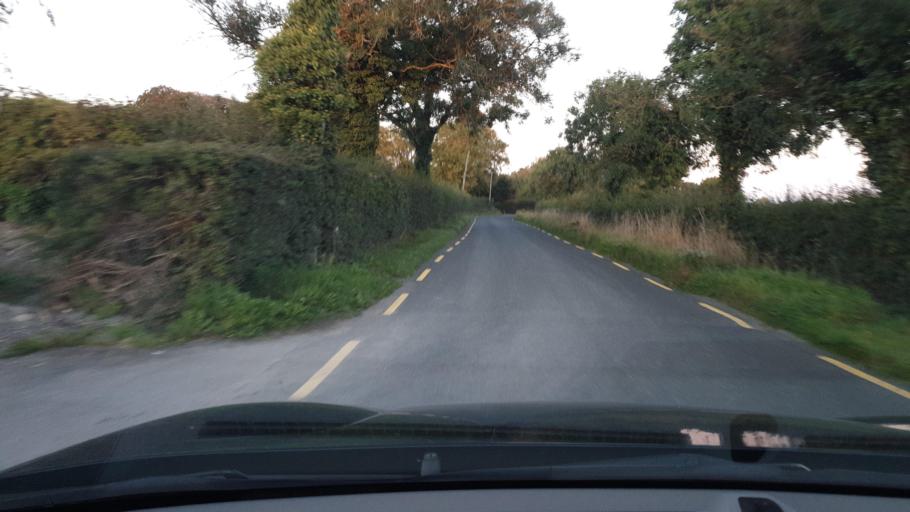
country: IE
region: Leinster
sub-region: Kildare
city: Prosperous
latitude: 53.3305
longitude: -6.7597
